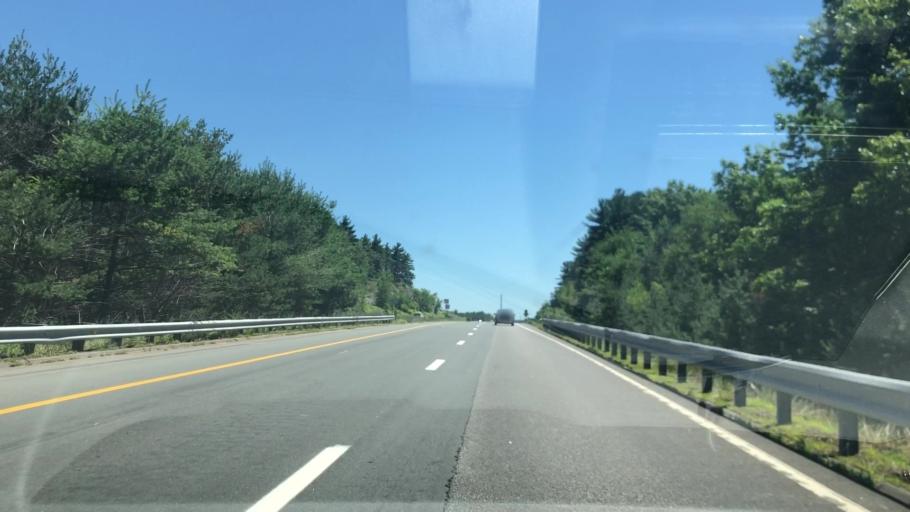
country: US
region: New Hampshire
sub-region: Hillsborough County
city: Manchester
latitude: 42.9584
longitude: -71.4096
